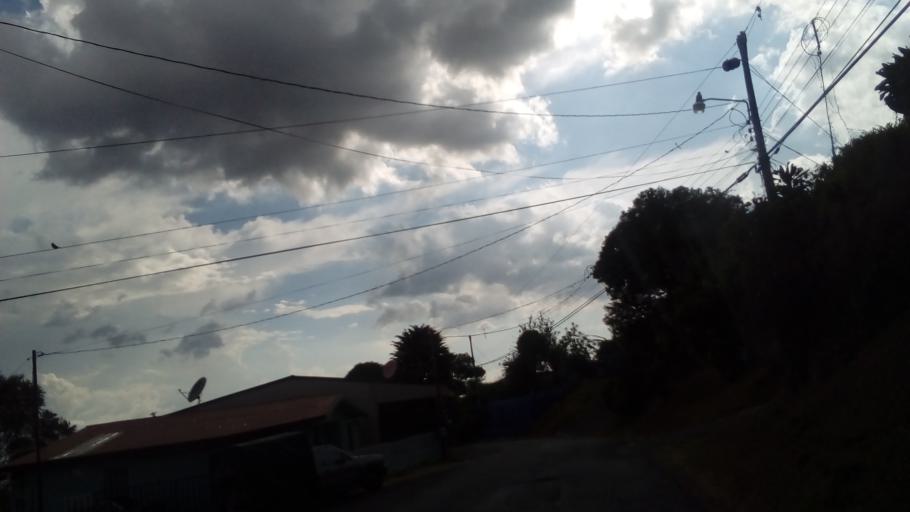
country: CR
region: Alajuela
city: San Juan
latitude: 10.1098
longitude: -84.2691
